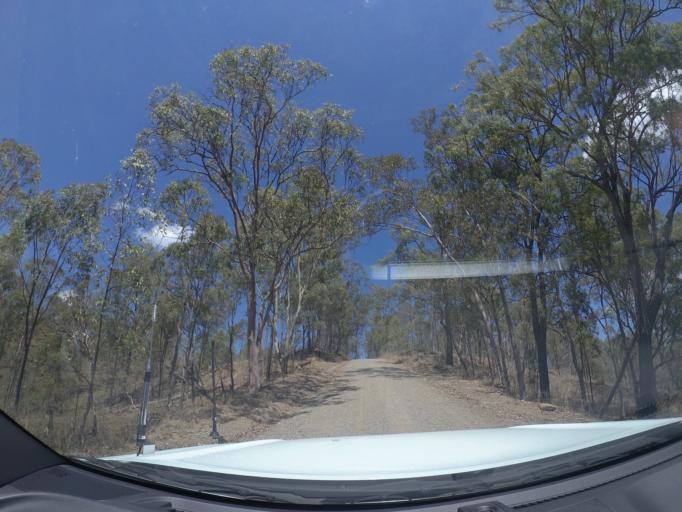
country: AU
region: Queensland
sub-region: Ipswich
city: Deebing Heights
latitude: -27.8273
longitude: 152.8358
